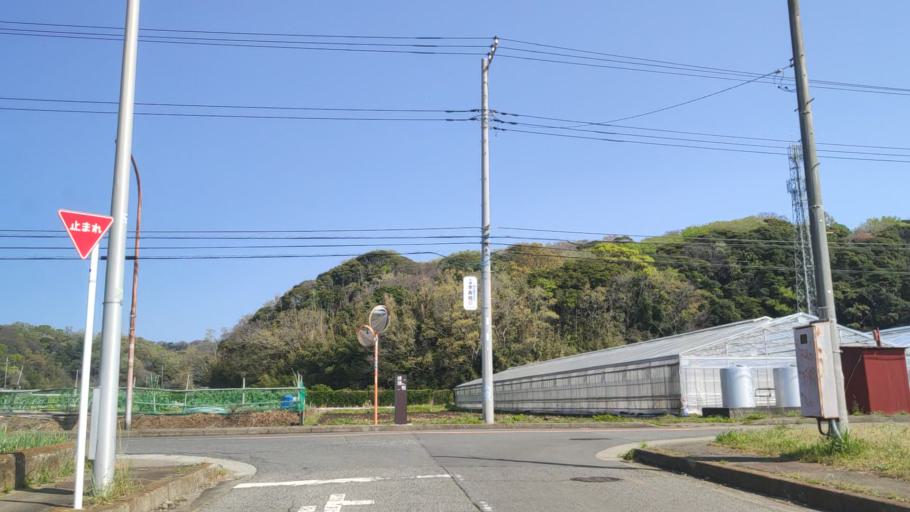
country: JP
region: Kanagawa
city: Oiso
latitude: 35.3092
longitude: 139.2966
